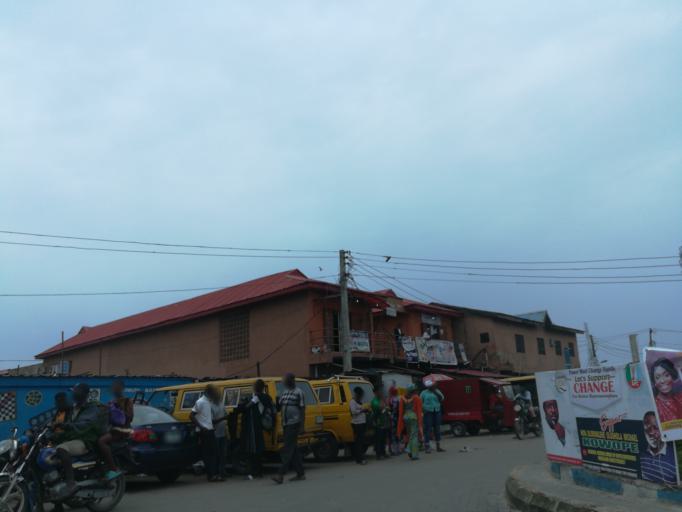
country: NG
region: Lagos
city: Makoko
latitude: 6.4992
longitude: 3.3869
